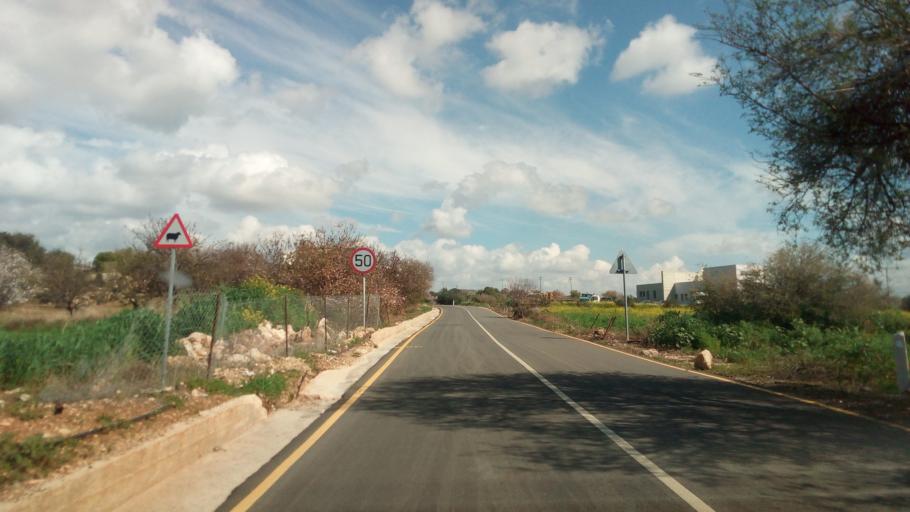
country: CY
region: Pafos
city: Mesogi
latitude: 34.7422
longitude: 32.5424
